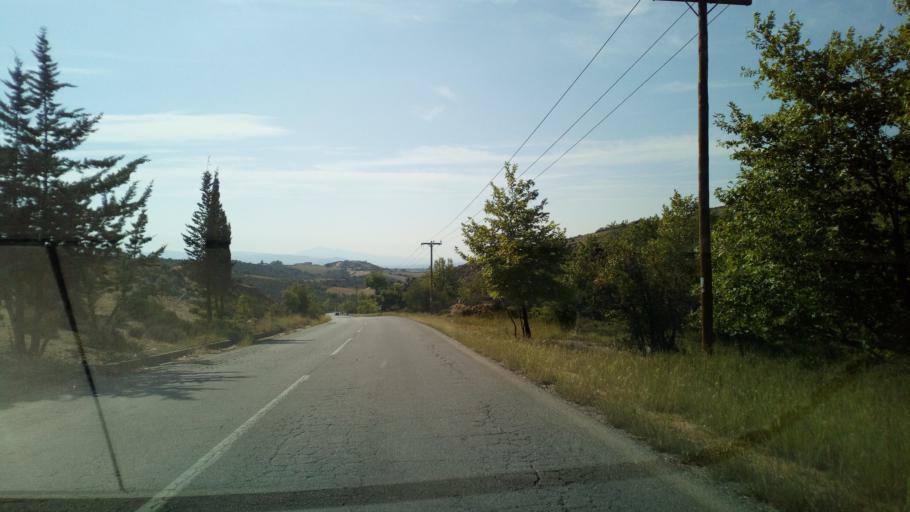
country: GR
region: Central Macedonia
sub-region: Nomos Chalkidikis
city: Arnaia
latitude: 40.5004
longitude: 23.4915
